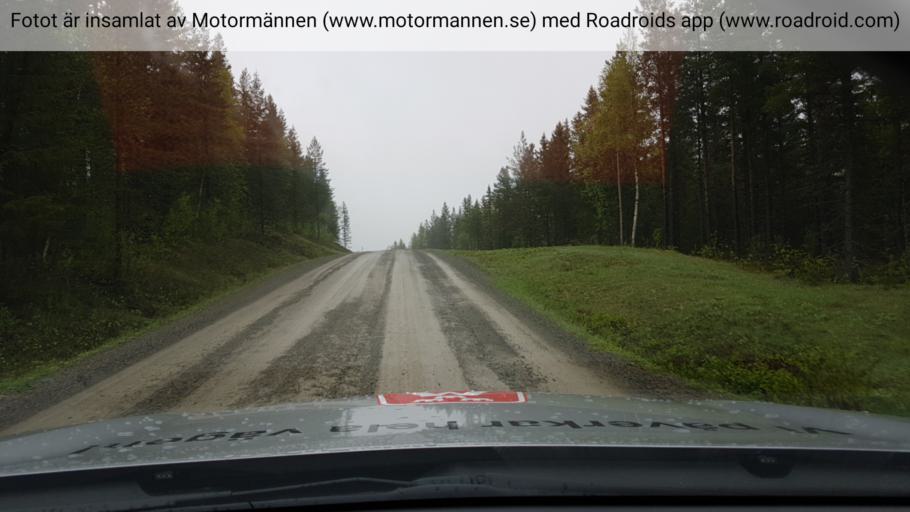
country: SE
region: Jaemtland
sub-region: Bergs Kommun
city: Hoverberg
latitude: 62.9964
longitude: 14.1537
